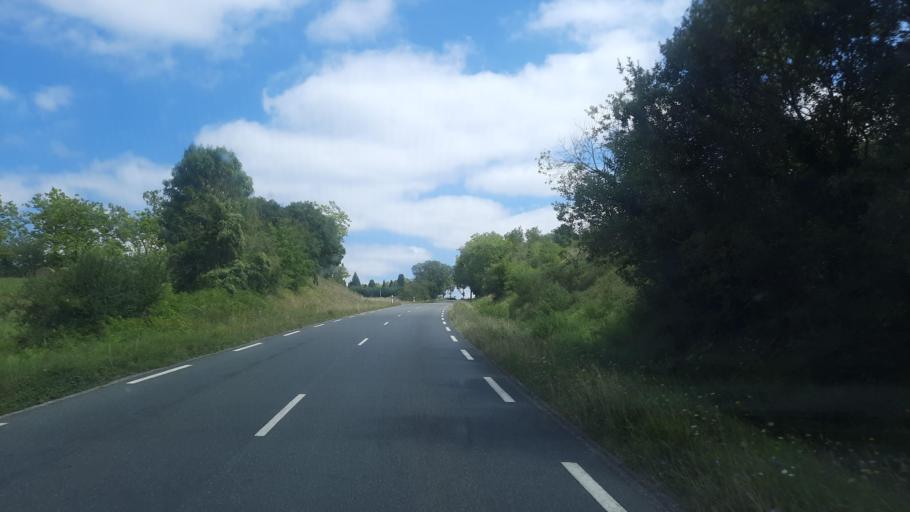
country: FR
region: Midi-Pyrenees
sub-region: Departement de la Haute-Garonne
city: Boulogne-sur-Gesse
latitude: 43.2903
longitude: 0.6354
